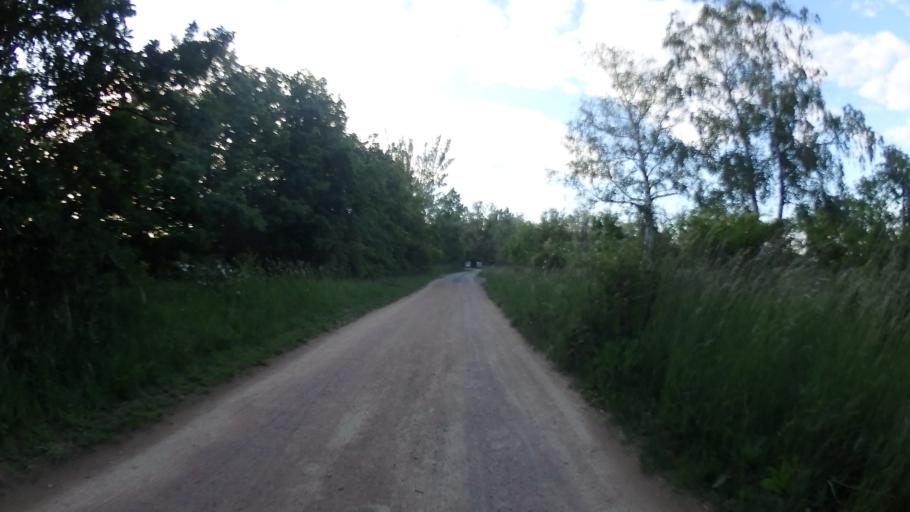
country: CZ
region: South Moravian
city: Ostopovice
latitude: 49.1519
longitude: 16.5451
